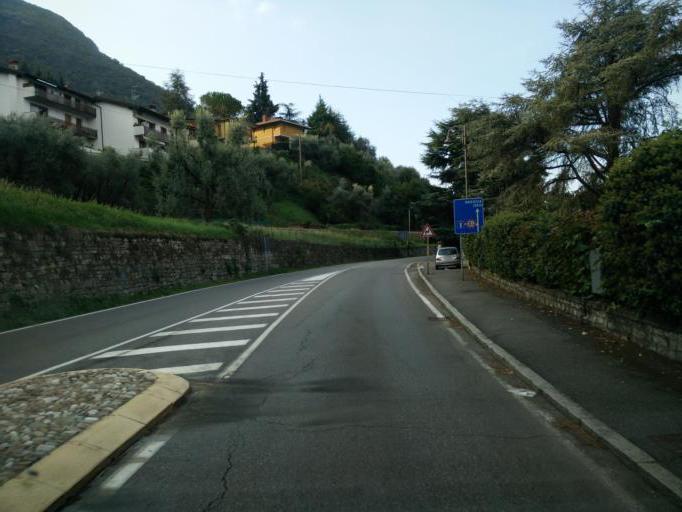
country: IT
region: Lombardy
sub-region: Provincia di Brescia
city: Sulzano
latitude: 45.6861
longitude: 10.0978
